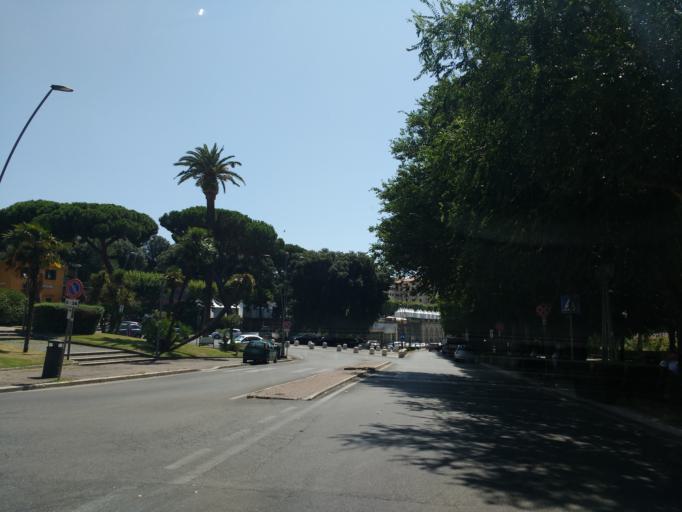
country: IT
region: Latium
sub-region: Citta metropolitana di Roma Capitale
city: Armetta
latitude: 41.8066
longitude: 12.6796
